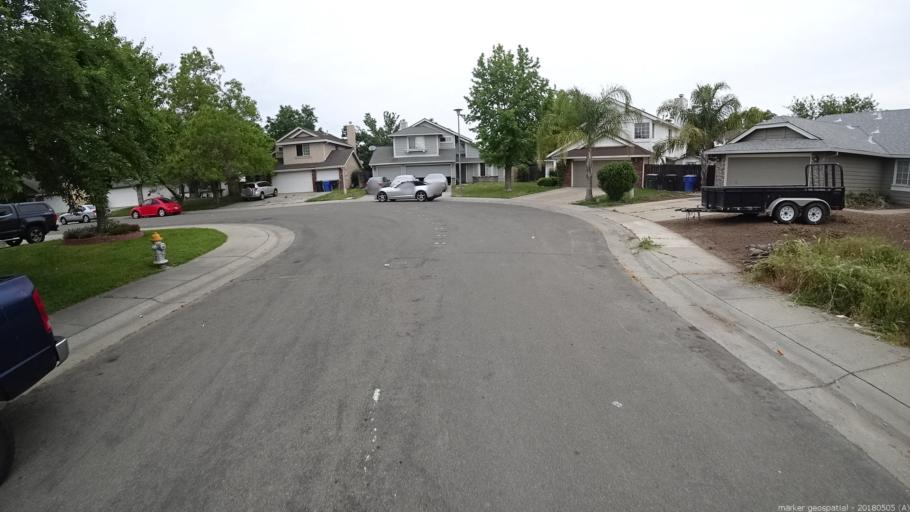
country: US
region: California
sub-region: Sacramento County
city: Rio Linda
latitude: 38.6488
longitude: -121.4416
